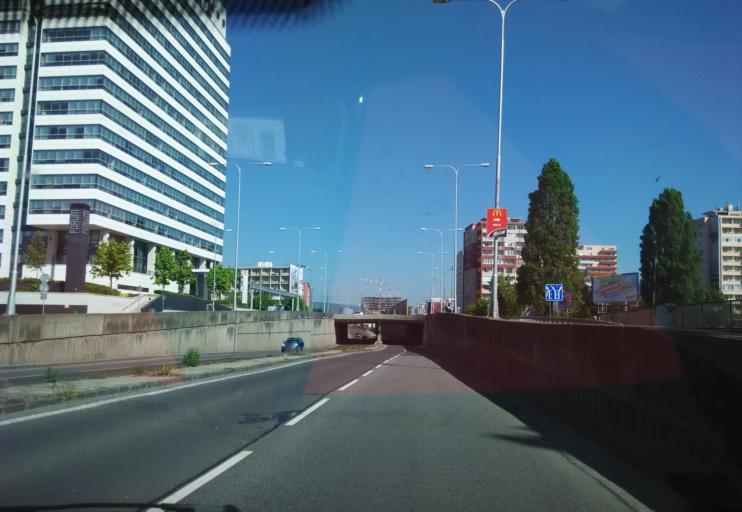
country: SK
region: Bratislavsky
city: Bratislava
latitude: 48.1473
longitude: 17.1504
